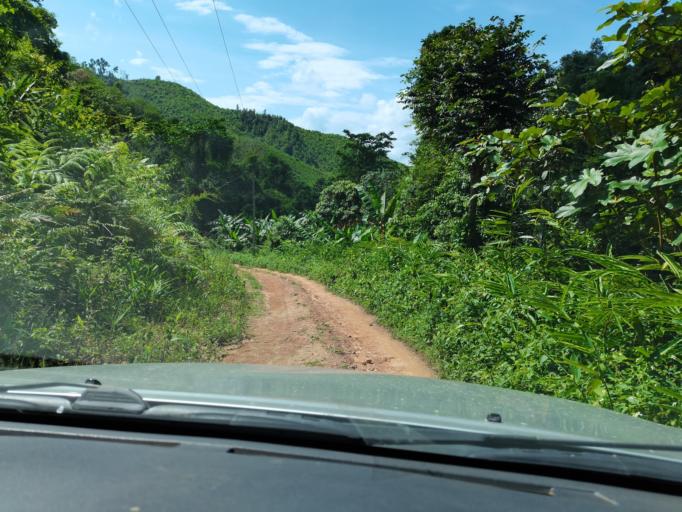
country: LA
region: Loungnamtha
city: Muang Nale
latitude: 20.5461
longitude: 101.0643
